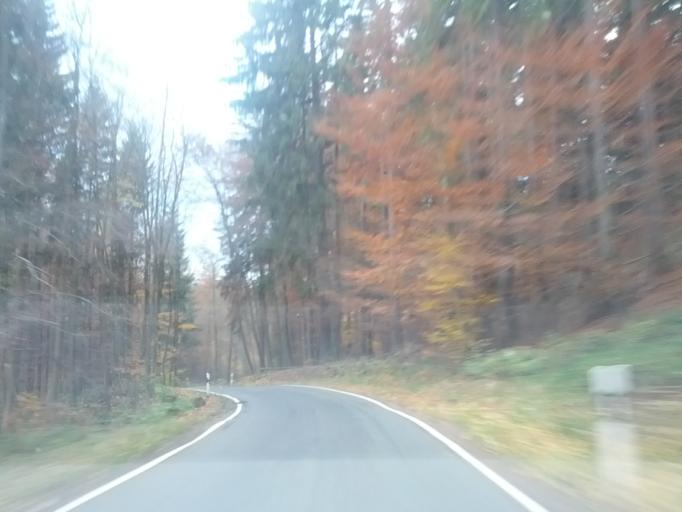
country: DE
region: Thuringia
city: Ruhla
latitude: 50.8947
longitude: 10.3230
